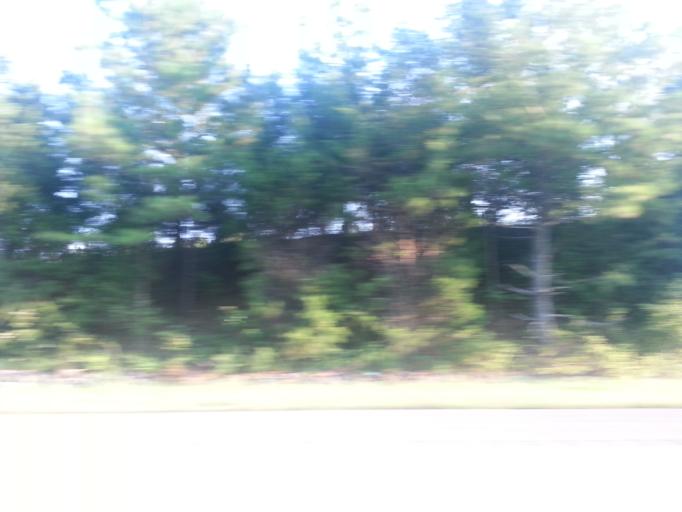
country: US
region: Tennessee
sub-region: McMinn County
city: Athens
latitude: 35.5207
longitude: -84.6438
